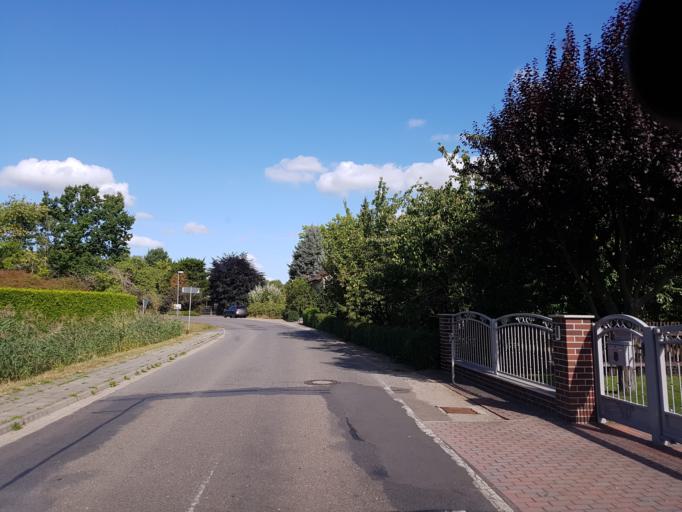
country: DE
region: Brandenburg
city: Sonnewalde
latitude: 51.6970
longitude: 13.6490
